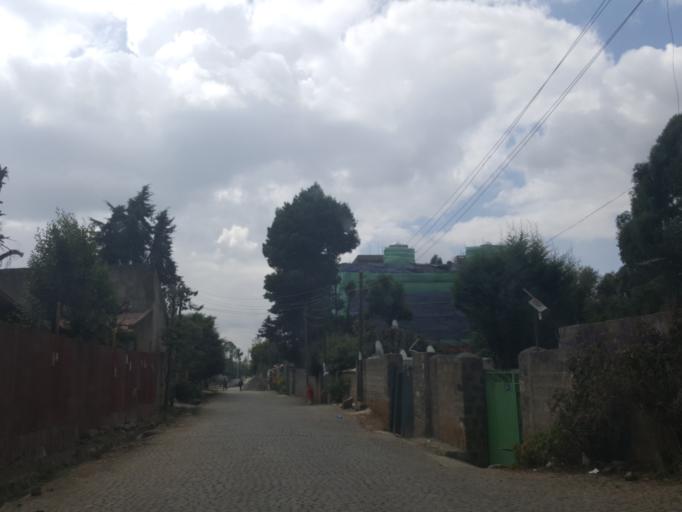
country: ET
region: Adis Abeba
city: Addis Ababa
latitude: 9.0577
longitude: 38.7174
